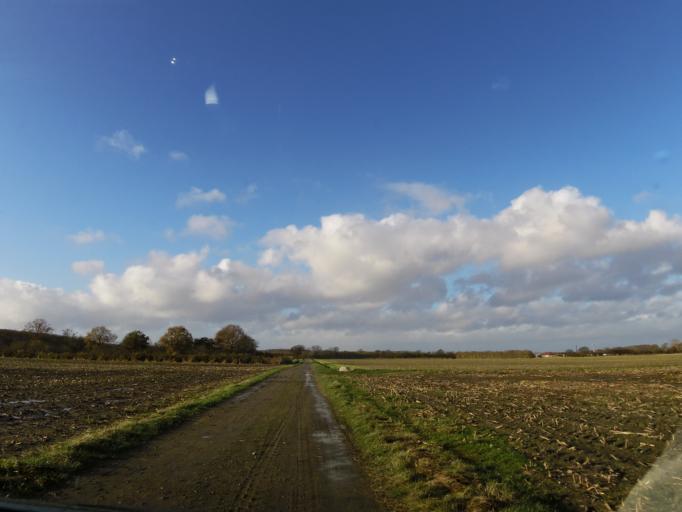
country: DK
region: Central Jutland
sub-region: Odder Kommune
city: Odder
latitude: 55.8482
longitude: 10.1863
